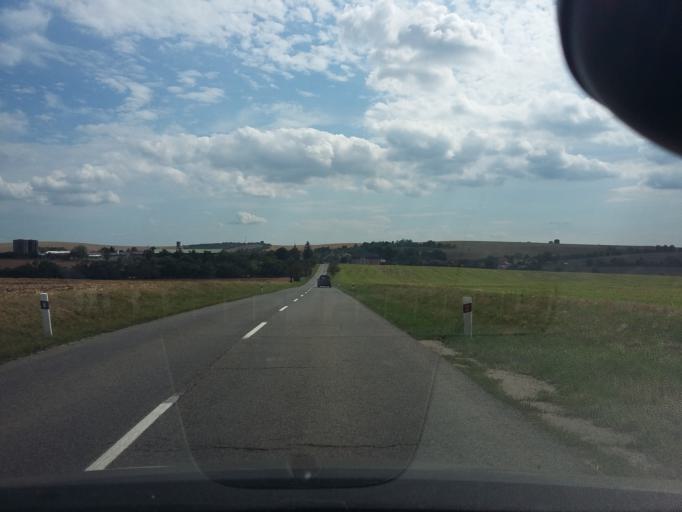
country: SK
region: Trnavsky
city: Gbely
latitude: 48.7311
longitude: 17.1641
